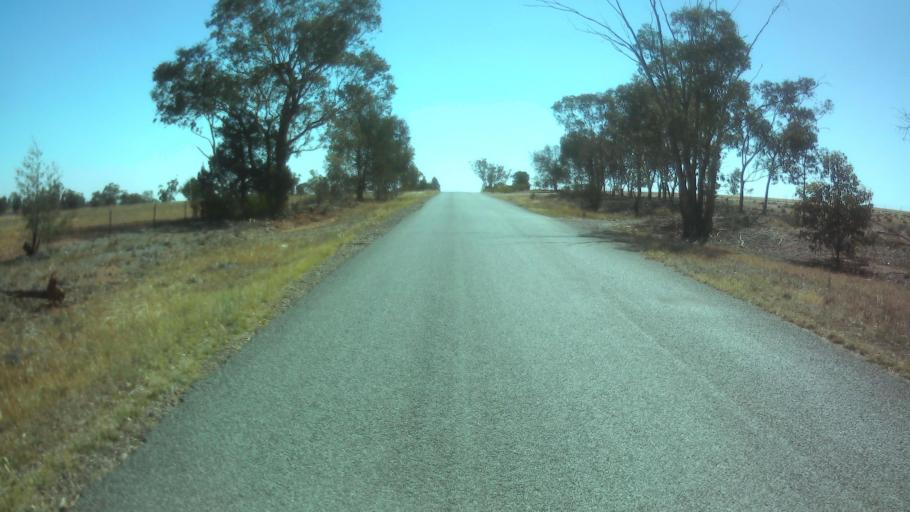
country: AU
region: New South Wales
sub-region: Weddin
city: Grenfell
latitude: -33.7537
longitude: 147.8394
